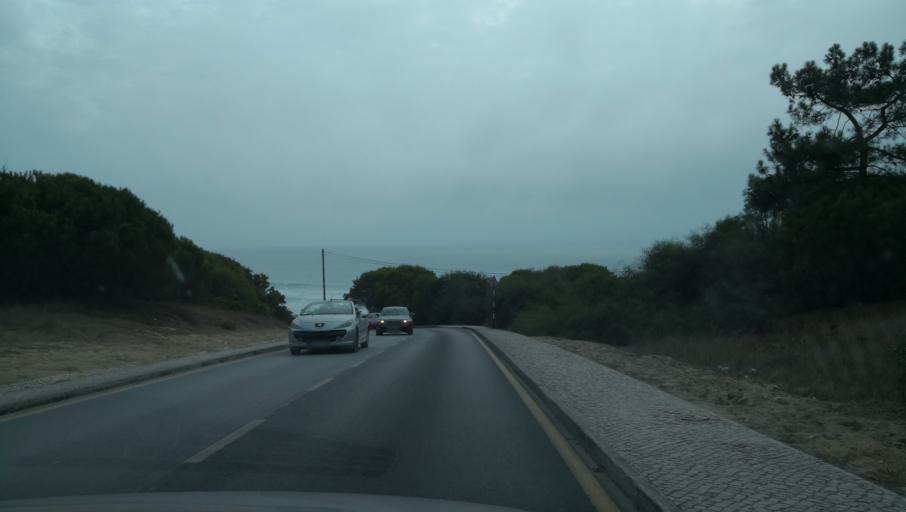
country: PT
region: Setubal
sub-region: Almada
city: Charneca
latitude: 38.5756
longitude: -9.1938
